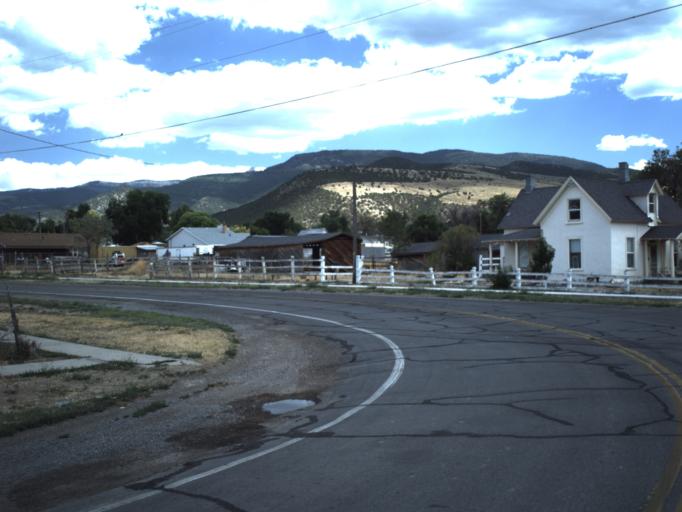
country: US
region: Utah
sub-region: Sanpete County
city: Centerfield
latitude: 39.1159
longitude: -111.7108
